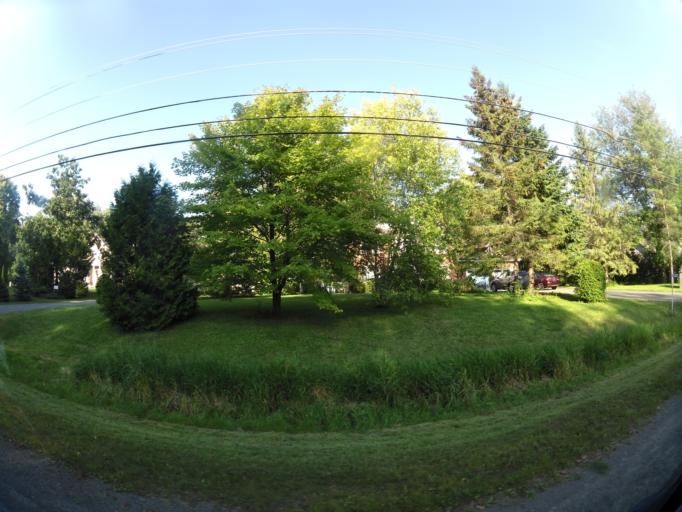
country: CA
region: Ontario
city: Clarence-Rockland
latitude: 45.5067
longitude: -75.4529
